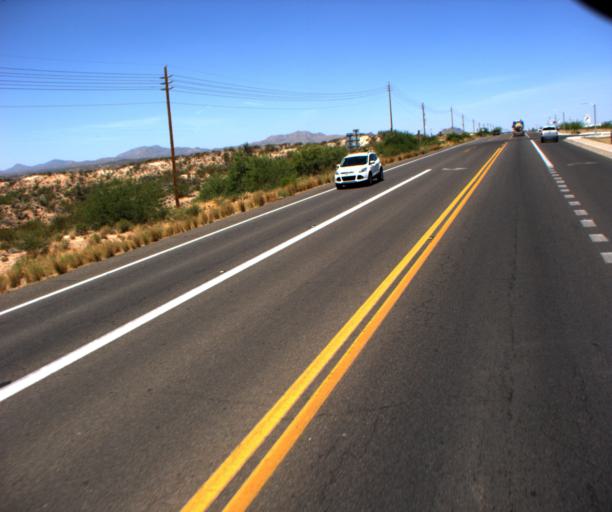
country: US
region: Arizona
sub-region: Gila County
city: Peridot
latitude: 33.2985
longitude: -110.4593
